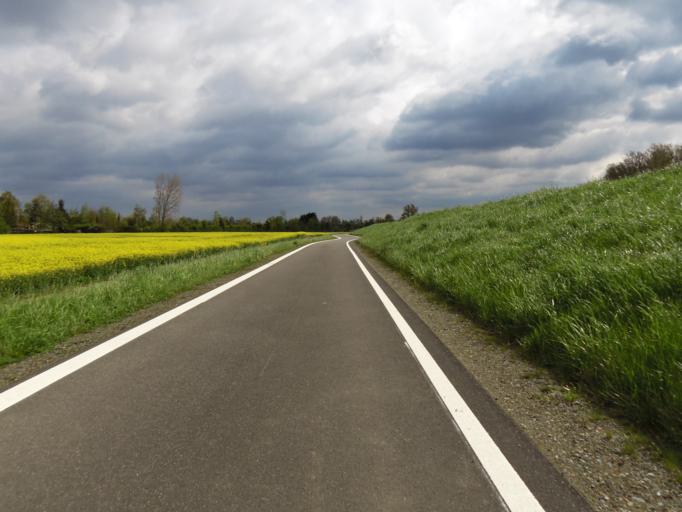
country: DE
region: Hesse
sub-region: Regierungsbezirk Darmstadt
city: Biblis
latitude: 49.6771
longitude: 8.4314
